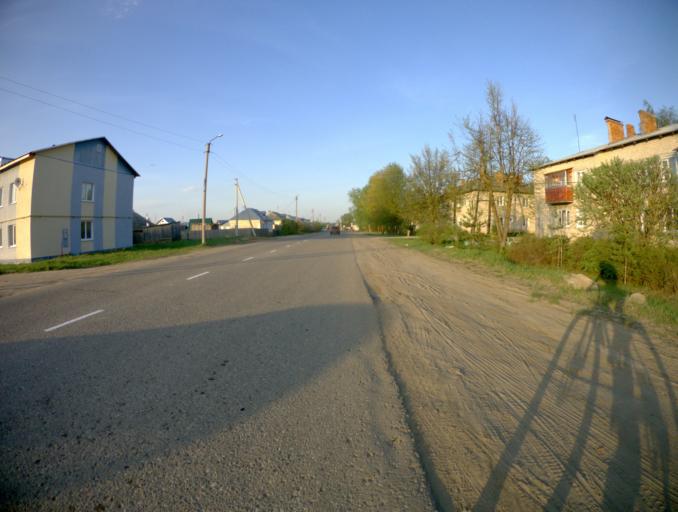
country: RU
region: Ivanovo
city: Yuzha
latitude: 56.5786
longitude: 41.9849
